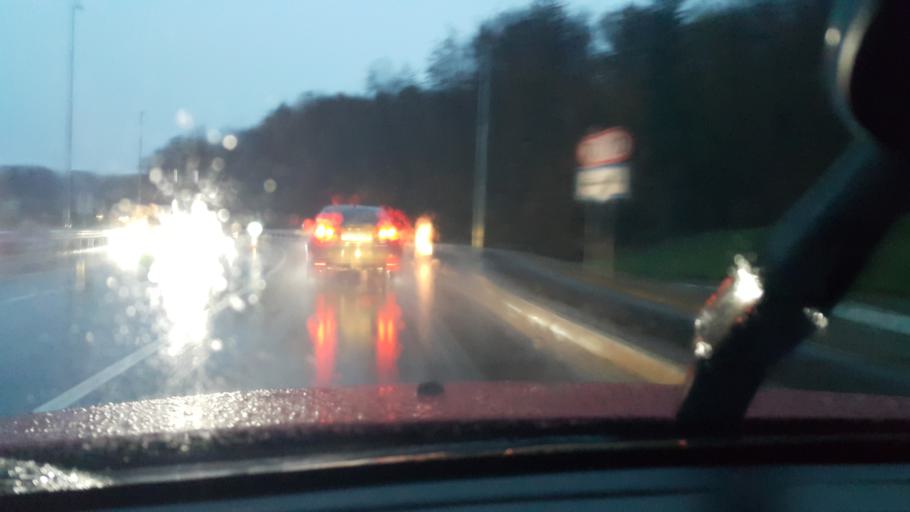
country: SI
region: Poljcane
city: Poljcane
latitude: 46.3275
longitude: 15.5756
